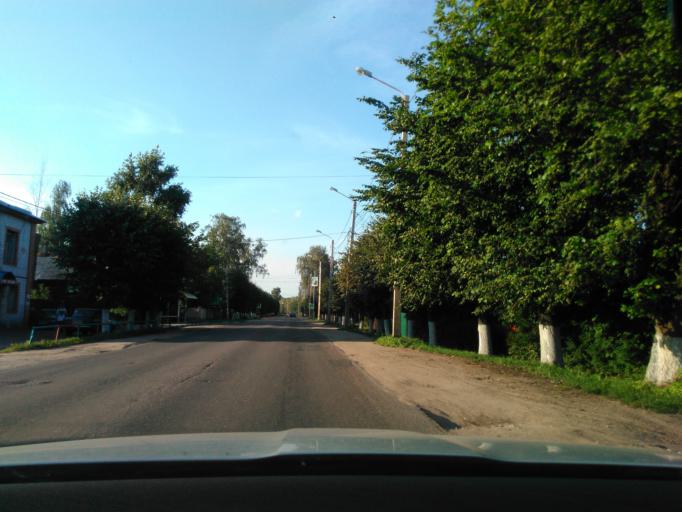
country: RU
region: Tverskaya
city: Konakovo
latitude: 56.7034
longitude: 36.7686
